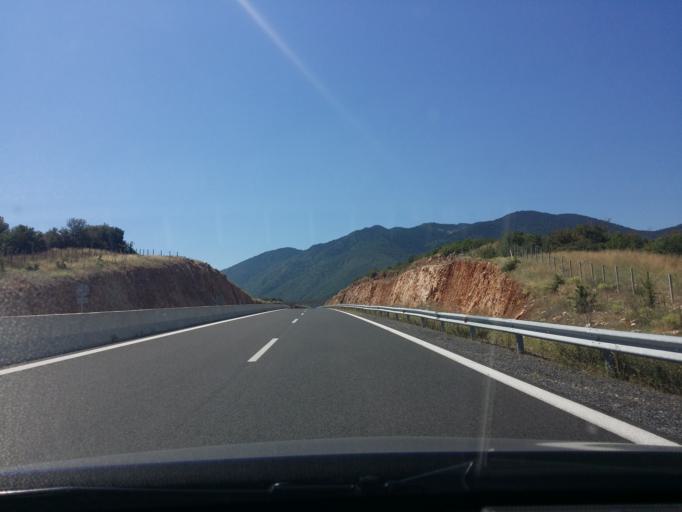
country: GR
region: Peloponnese
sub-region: Nomos Arkadias
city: Megalopoli
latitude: 37.2923
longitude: 22.2124
